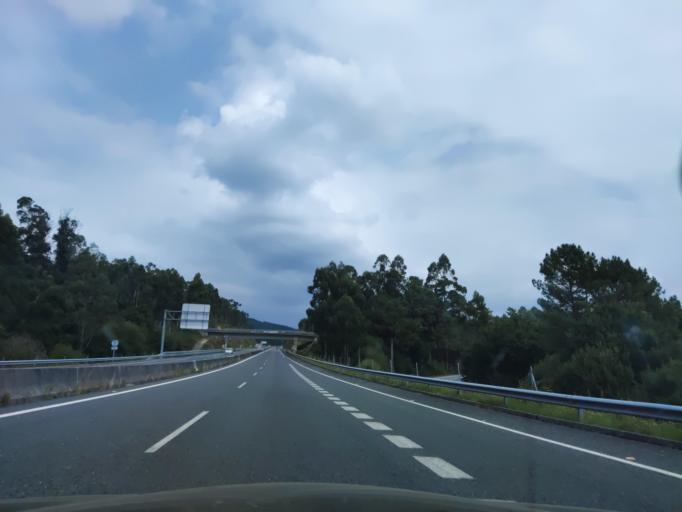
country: ES
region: Galicia
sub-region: Provincia de Pontevedra
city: Catoira
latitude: 42.6853
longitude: -8.7438
